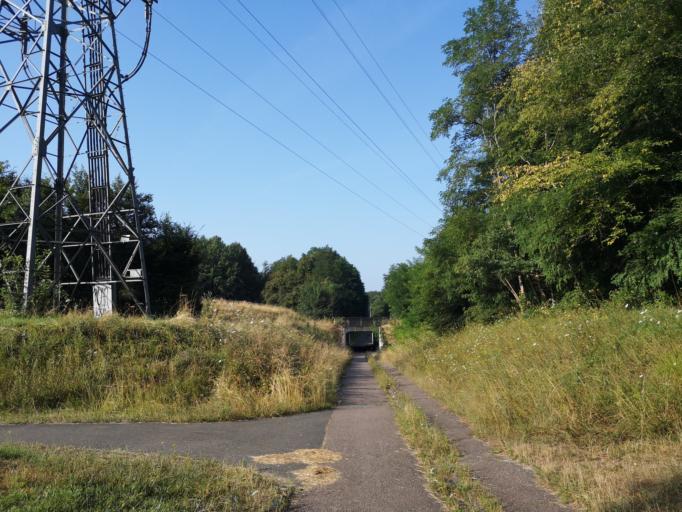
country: FR
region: Centre
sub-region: Departement du Loiret
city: Saint-Jean-de-Braye
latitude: 47.9262
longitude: 1.9846
